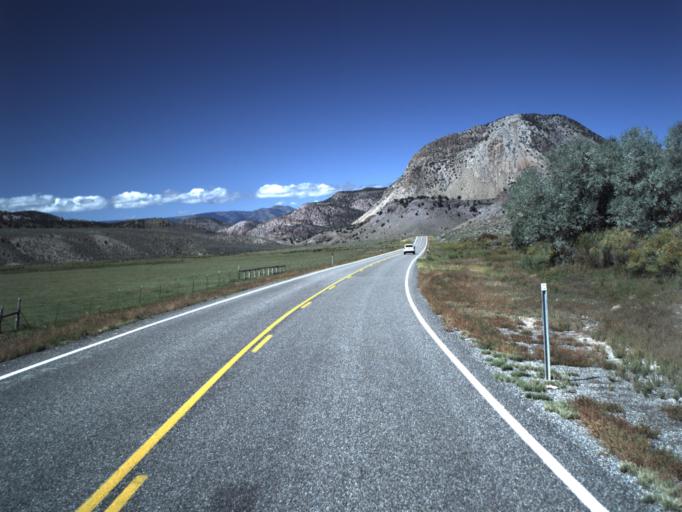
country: US
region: Utah
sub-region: Piute County
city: Junction
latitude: 38.1691
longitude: -112.0563
